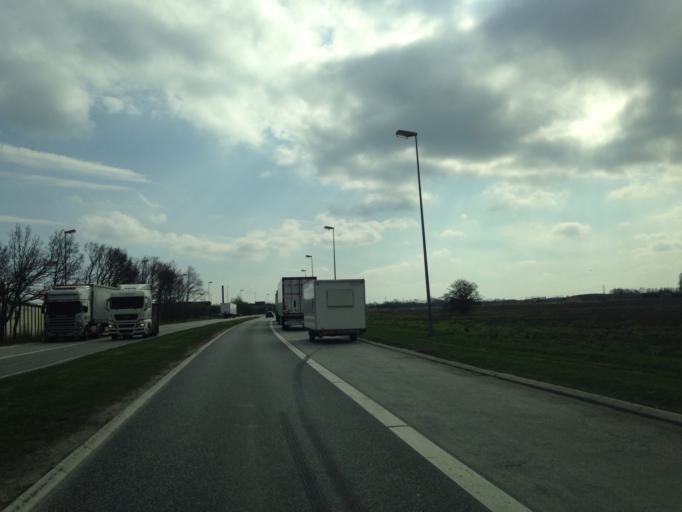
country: DK
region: Capital Region
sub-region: Ishoj Kommune
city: Ishoj
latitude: 55.6199
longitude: 12.3188
